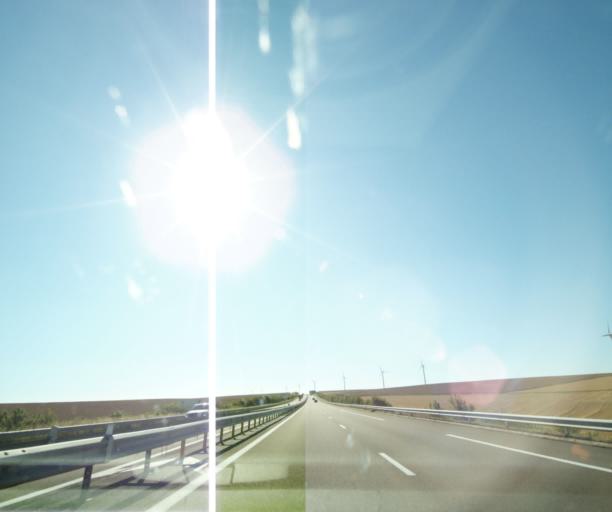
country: FR
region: Champagne-Ardenne
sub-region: Departement de l'Aube
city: Vendeuvre-sur-Barse
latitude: 48.1688
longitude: 4.4804
